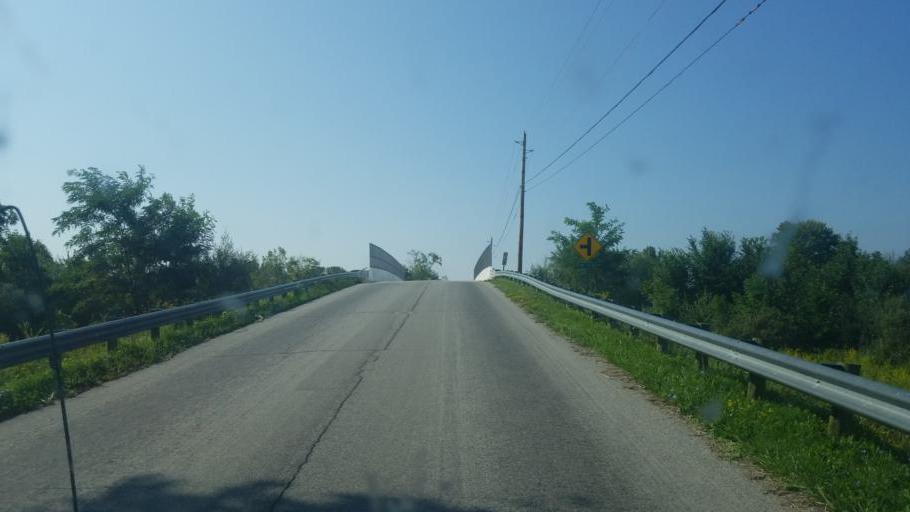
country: US
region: Ohio
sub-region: Wayne County
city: West Salem
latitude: 41.0409
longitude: -82.2017
